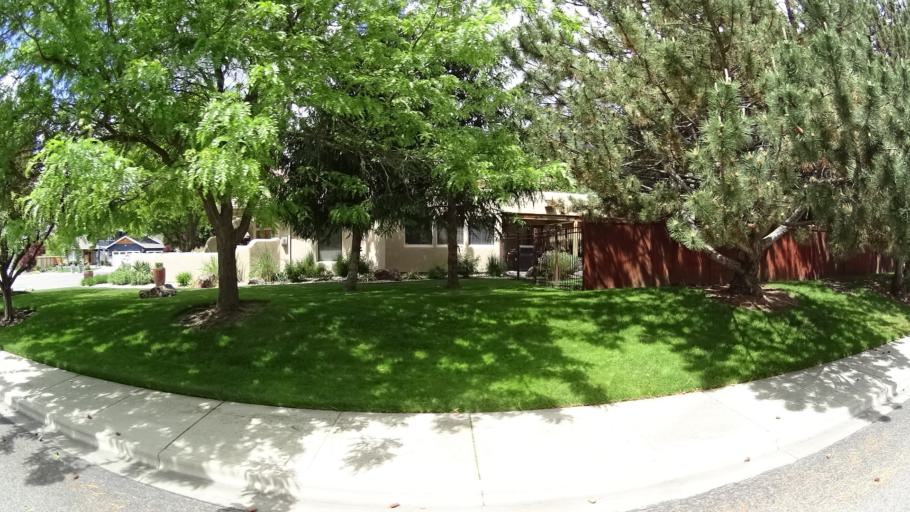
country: US
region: Idaho
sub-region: Ada County
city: Garden City
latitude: 43.6659
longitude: -116.2169
